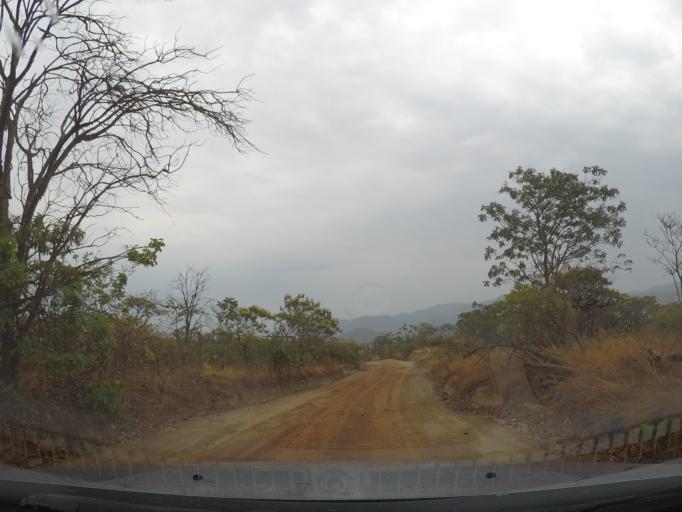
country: BR
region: Goias
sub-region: Pirenopolis
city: Pirenopolis
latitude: -15.8303
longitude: -48.9057
